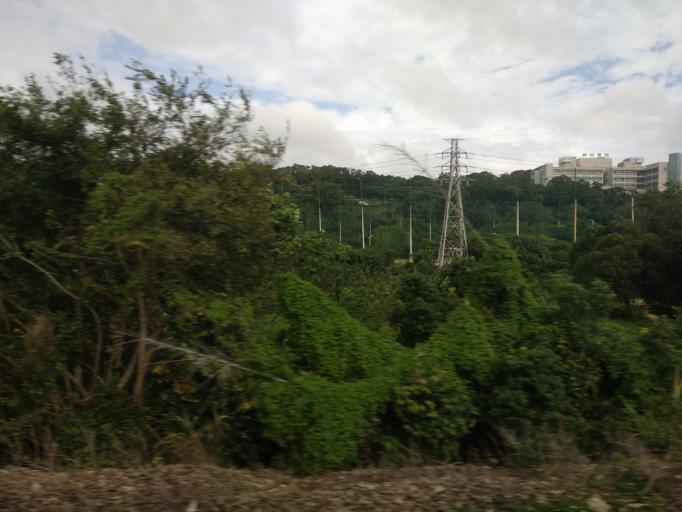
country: TW
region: Taiwan
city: Daxi
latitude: 24.9139
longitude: 121.1535
